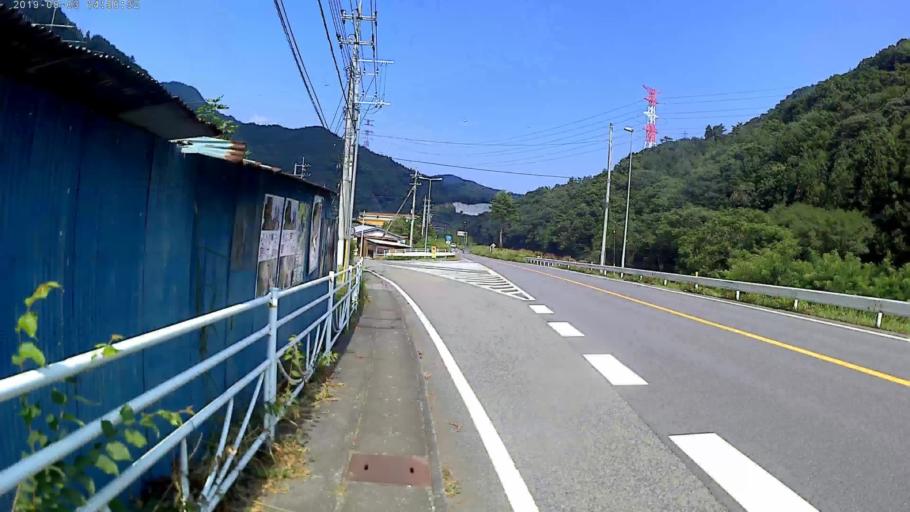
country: JP
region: Yamanashi
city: Otsuki
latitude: 35.6020
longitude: 138.8515
